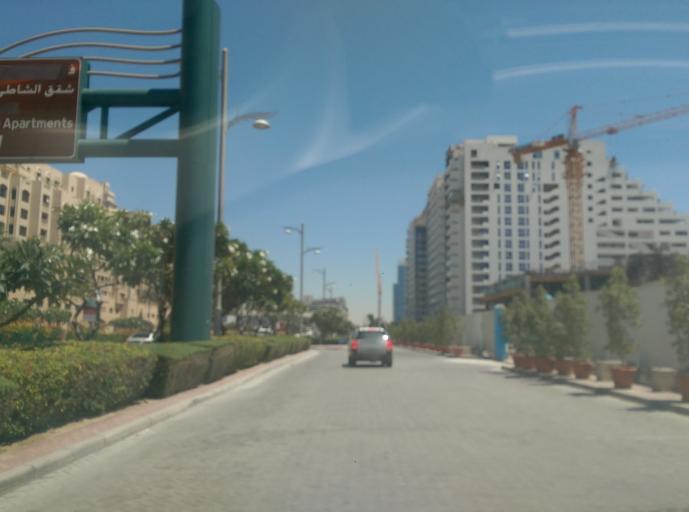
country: AE
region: Dubai
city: Dubai
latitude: 25.1064
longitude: 55.1468
